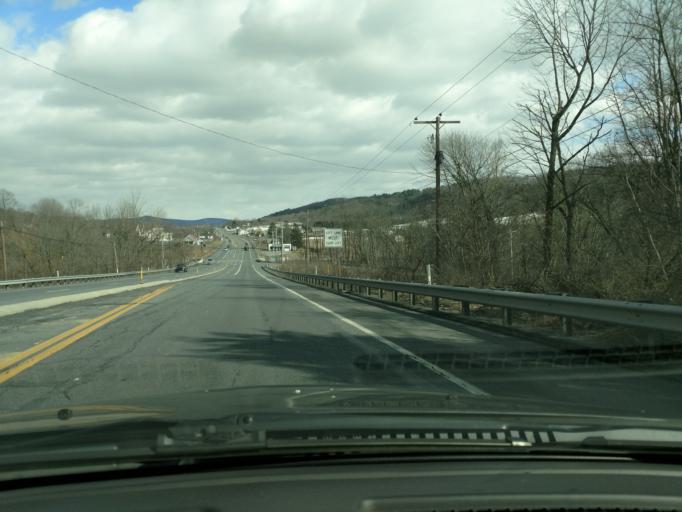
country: US
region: Pennsylvania
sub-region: Schuylkill County
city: Orwigsburg
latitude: 40.6420
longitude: -76.1081
